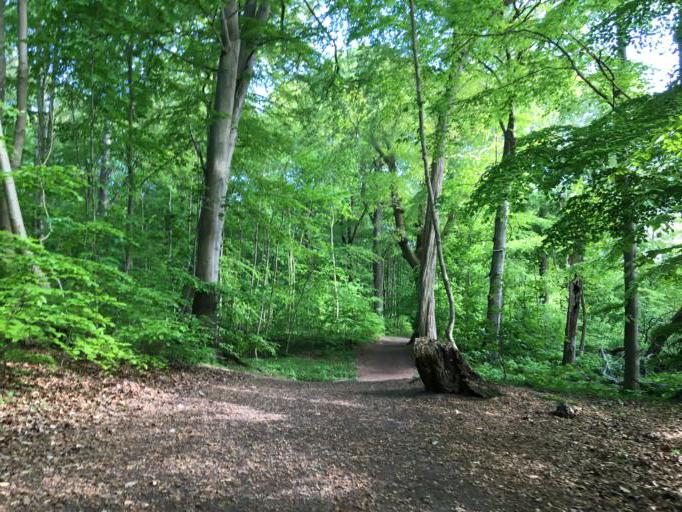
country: DK
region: Capital Region
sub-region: Hillerod Kommune
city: Hillerod
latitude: 55.9263
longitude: 12.3171
